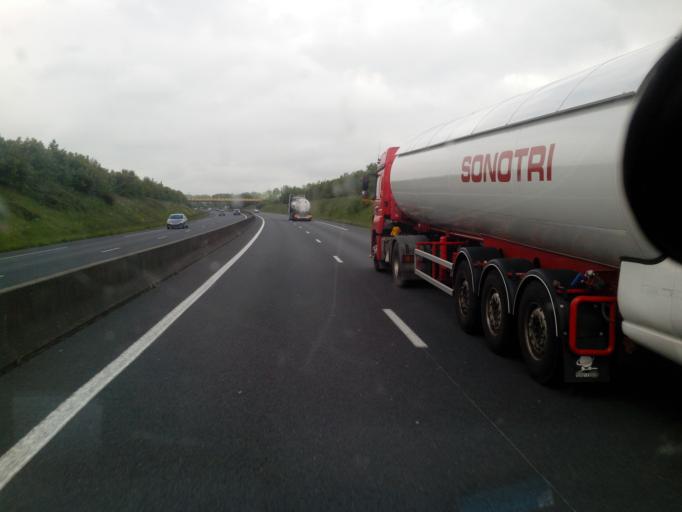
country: FR
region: Lower Normandy
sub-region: Departement du Calvados
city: Villers-Bocage
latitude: 49.0752
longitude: -0.6434
